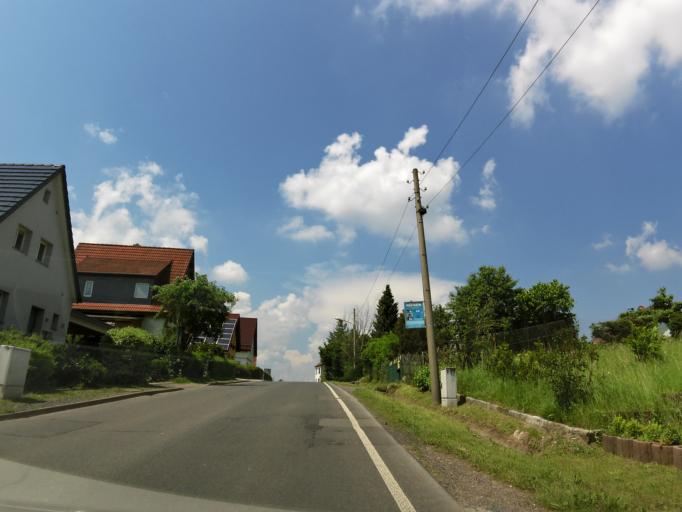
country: DE
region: Thuringia
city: Waltershausen
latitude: 50.8966
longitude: 10.5439
